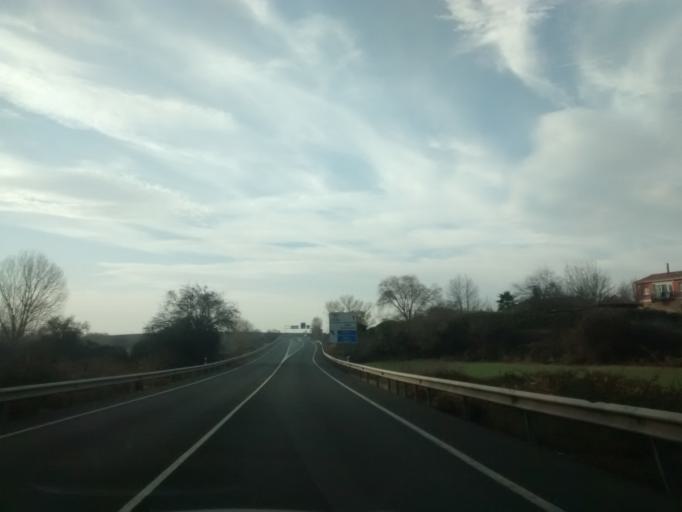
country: ES
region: La Rioja
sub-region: Provincia de La Rioja
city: Gimileo
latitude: 42.5474
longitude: -2.8251
